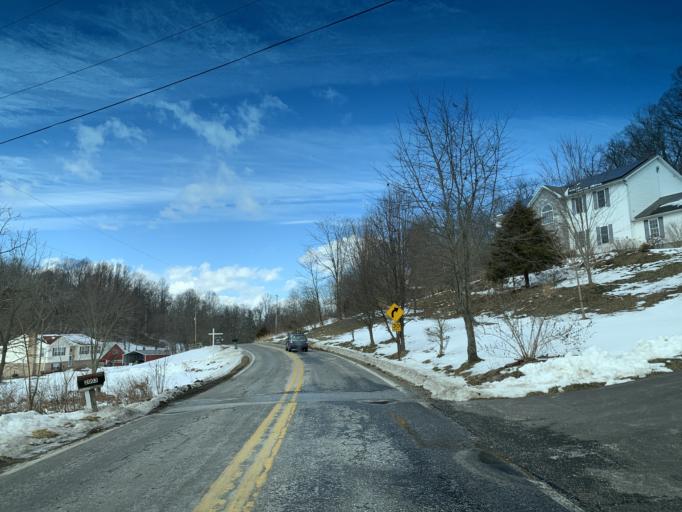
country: US
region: Pennsylvania
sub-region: York County
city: Shrewsbury
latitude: 39.7952
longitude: -76.6514
